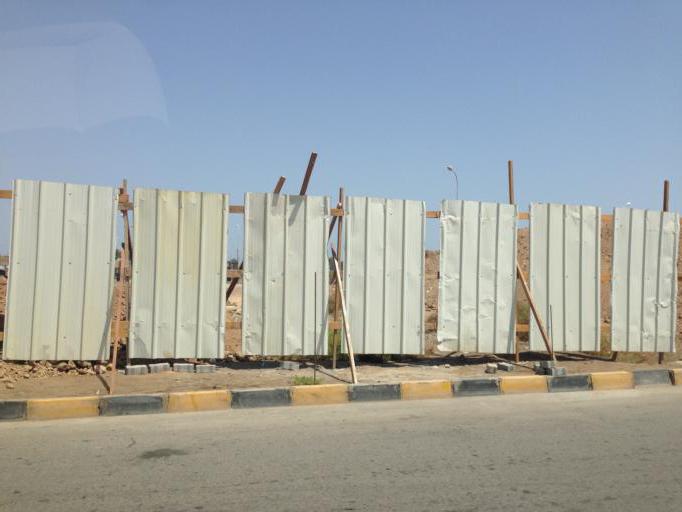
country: OM
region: Muhafazat Masqat
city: As Sib al Jadidah
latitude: 23.6251
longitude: 58.2622
